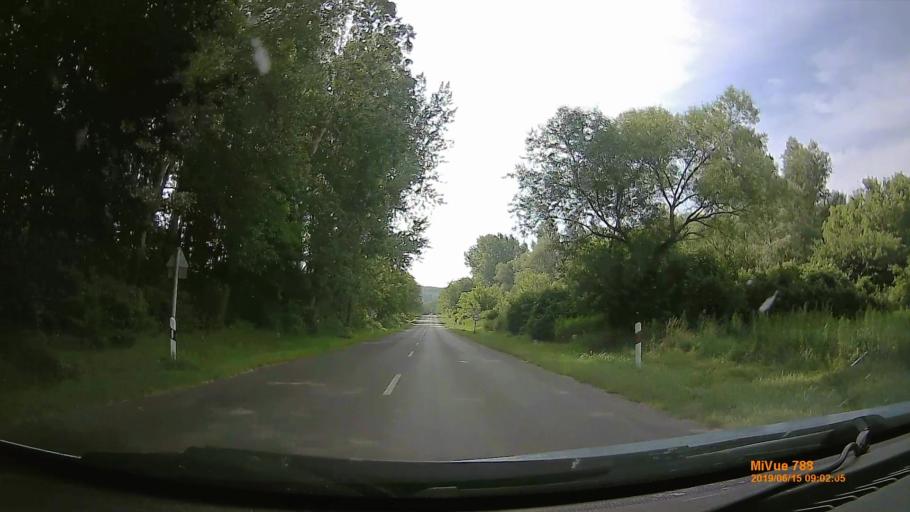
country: HU
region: Tolna
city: Iregszemcse
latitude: 46.7599
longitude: 18.1586
